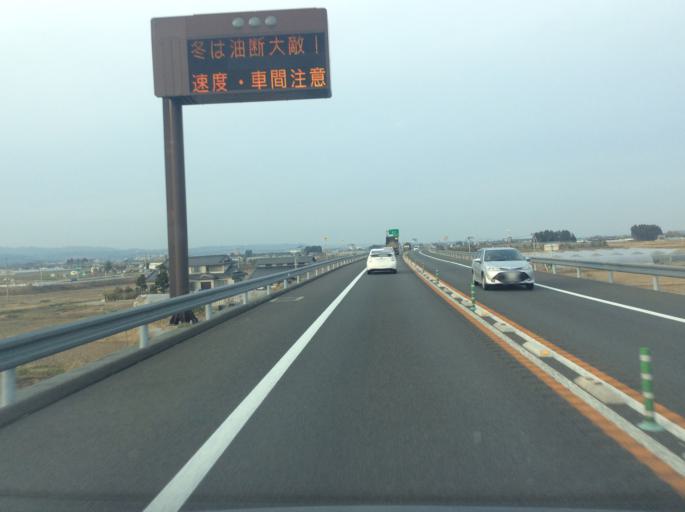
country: JP
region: Miyagi
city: Iwanuma
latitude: 38.0814
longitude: 140.8875
